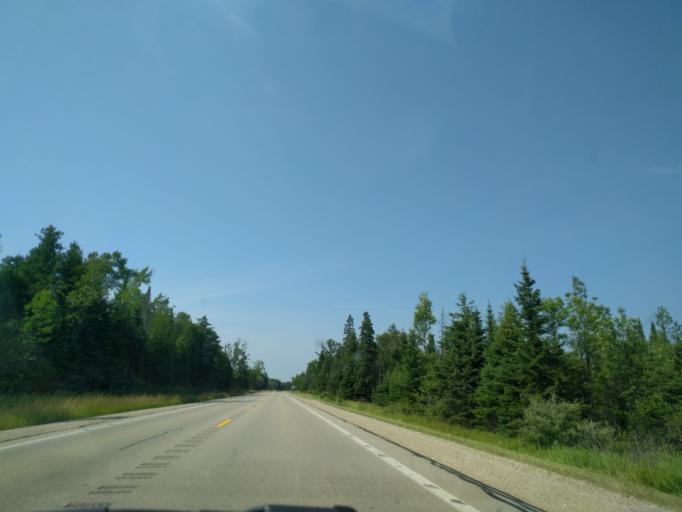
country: US
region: Michigan
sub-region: Delta County
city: Escanaba
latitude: 45.5148
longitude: -87.2882
